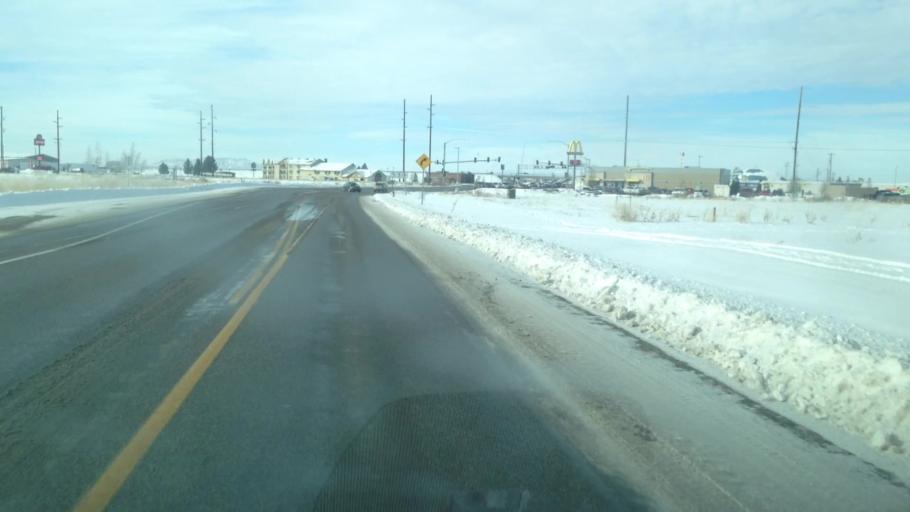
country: US
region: Idaho
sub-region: Madison County
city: Rexburg
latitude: 43.8035
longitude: -111.8055
